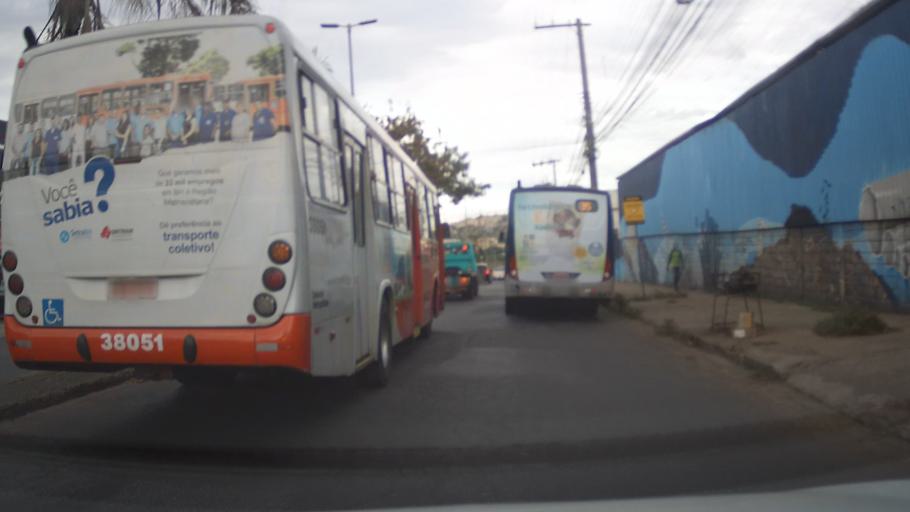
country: BR
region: Minas Gerais
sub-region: Contagem
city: Contagem
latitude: -19.9597
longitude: -44.0161
